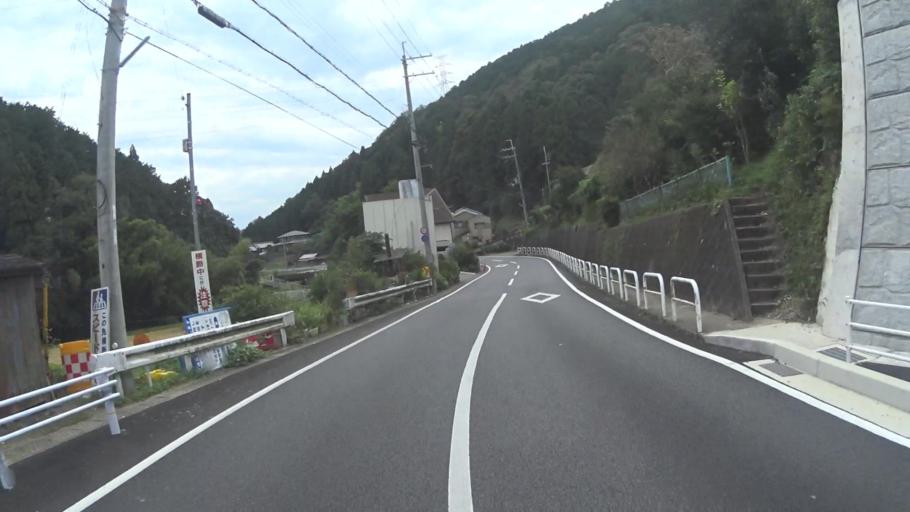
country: JP
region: Kyoto
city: Uji
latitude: 34.8691
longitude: 135.8731
